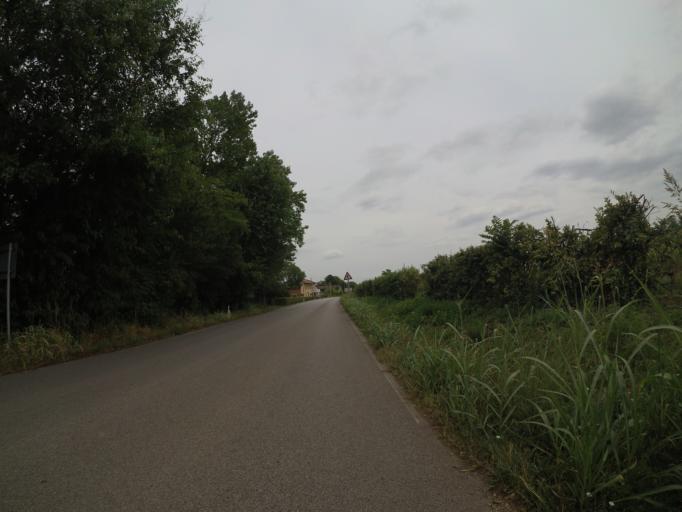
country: IT
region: Friuli Venezia Giulia
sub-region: Provincia di Udine
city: Colloredo di Prato
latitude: 46.0479
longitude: 13.1322
